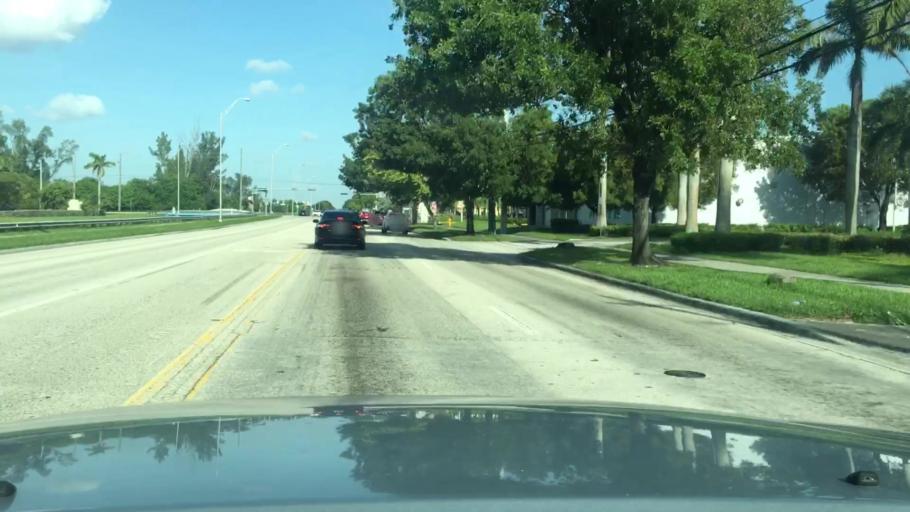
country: US
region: Florida
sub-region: Miami-Dade County
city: Doral
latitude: 25.7967
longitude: -80.3552
